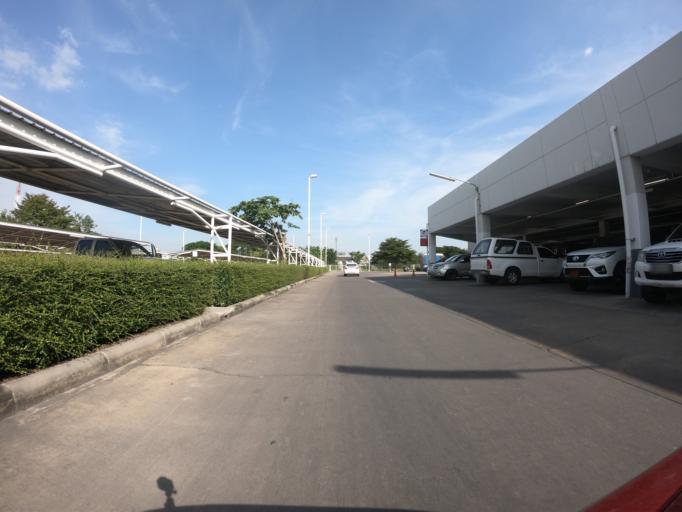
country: TH
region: Pathum Thani
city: Thanyaburi
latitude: 14.0268
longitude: 100.7432
